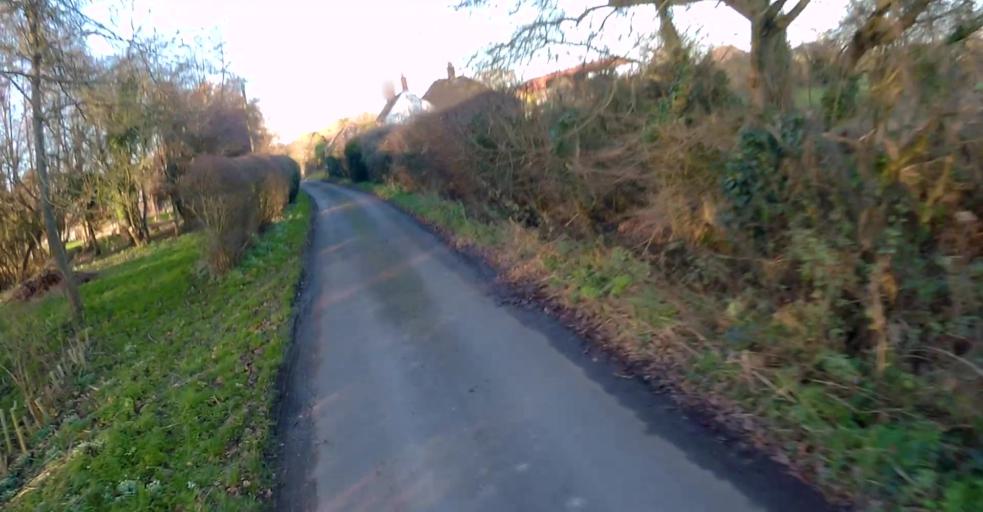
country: GB
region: England
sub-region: Hampshire
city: Hook
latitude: 51.3090
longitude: -1.0014
